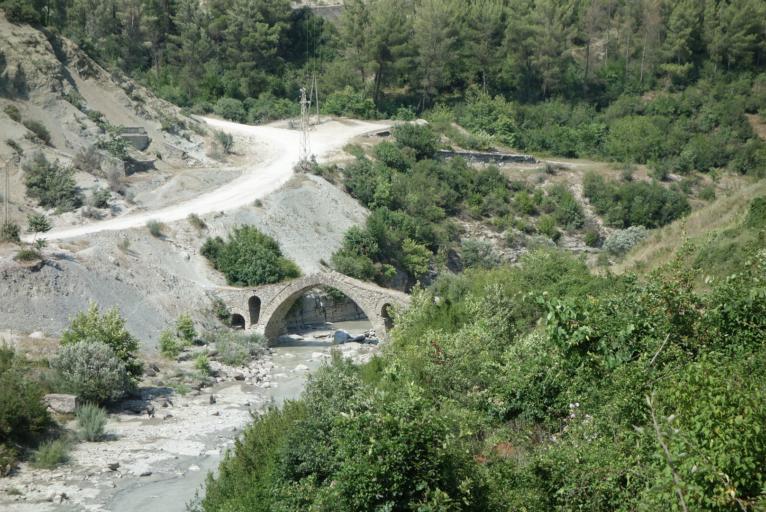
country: AL
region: Berat
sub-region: Rrethi i Skraparit
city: Corovode
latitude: 40.5142
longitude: 20.2415
